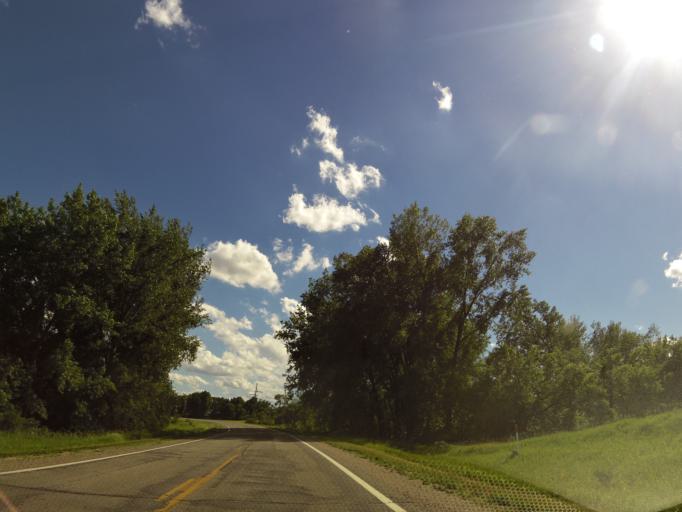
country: US
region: Minnesota
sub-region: Meeker County
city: Dassel
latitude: 45.1190
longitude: -94.2984
